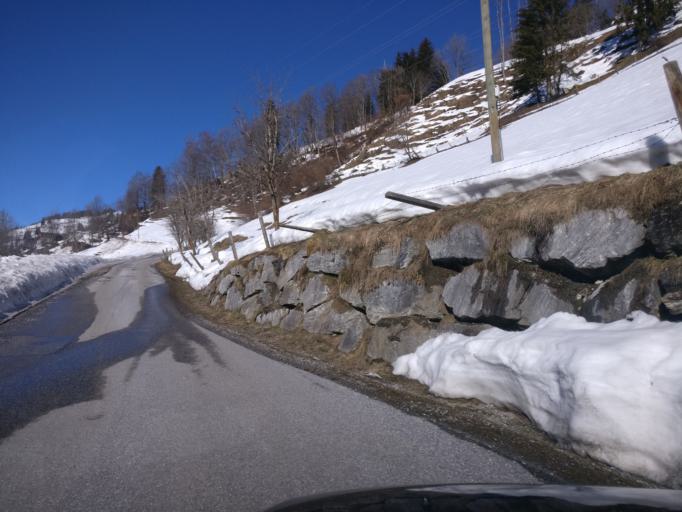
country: AT
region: Salzburg
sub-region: Politischer Bezirk Sankt Johann im Pongau
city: Wagrain
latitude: 47.3366
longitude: 13.2586
